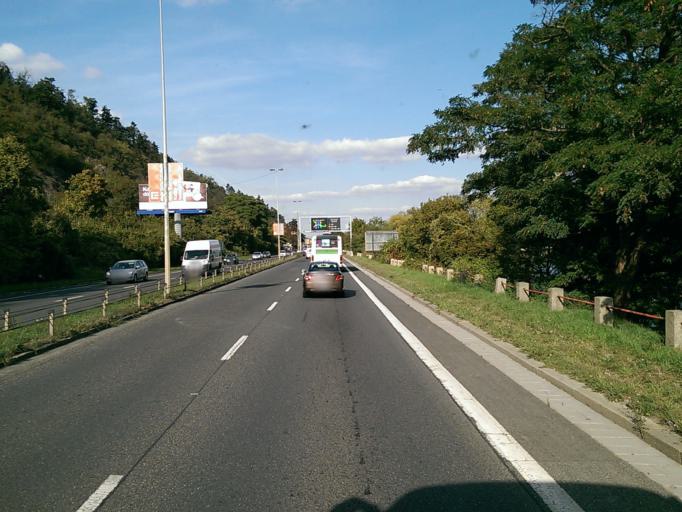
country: CZ
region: Praha
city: Branik
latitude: 50.0278
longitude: 14.3966
